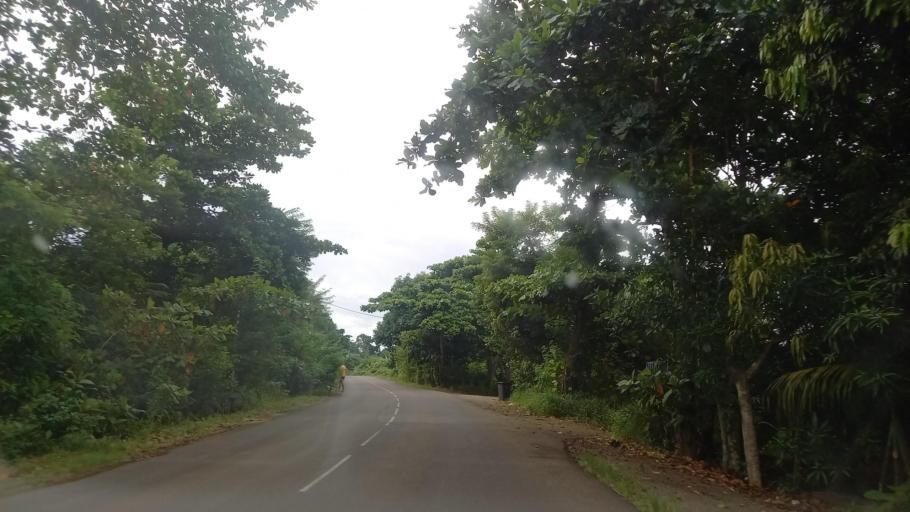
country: YT
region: Boueni
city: Boueni
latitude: -12.9162
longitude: 45.1019
